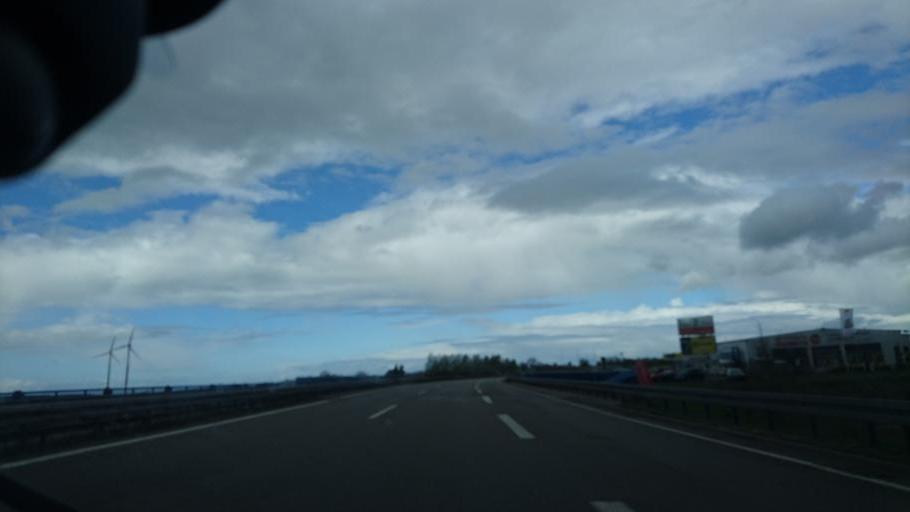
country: DE
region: Mecklenburg-Vorpommern
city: Stabelow
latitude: 54.0437
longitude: 12.0349
